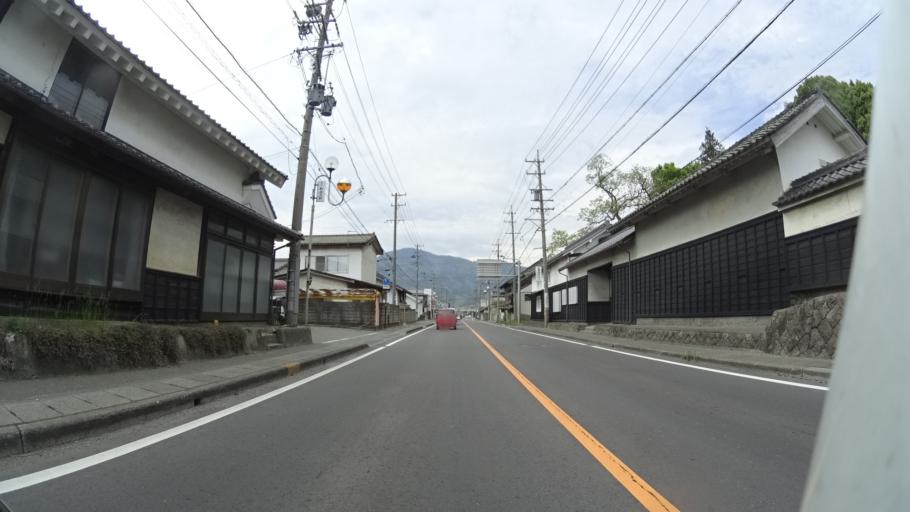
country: JP
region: Nagano
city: Ueda
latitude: 36.4466
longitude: 138.1897
